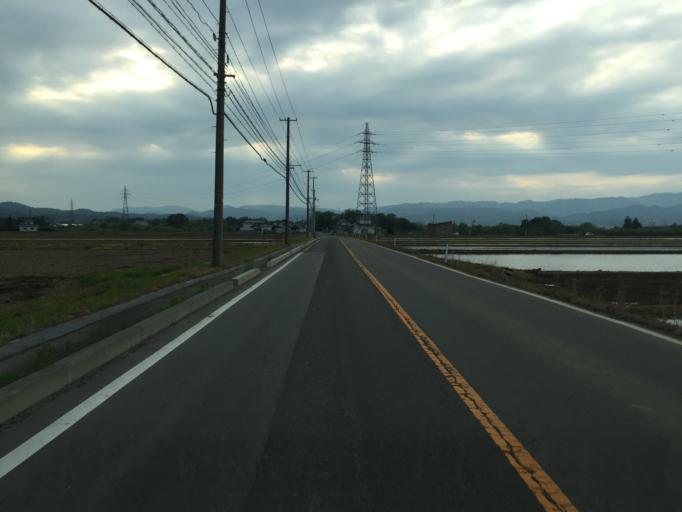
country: JP
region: Fukushima
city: Yanagawamachi-saiwaicho
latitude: 37.8744
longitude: 140.5660
